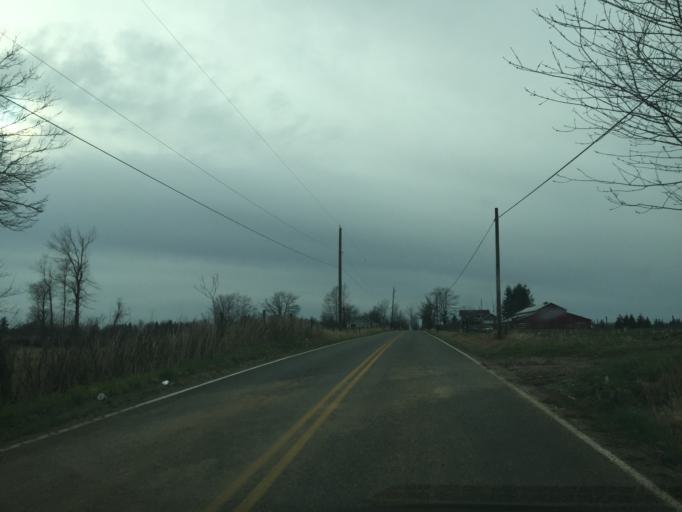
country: US
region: Washington
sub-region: Whatcom County
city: Everson
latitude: 48.9491
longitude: -122.3542
